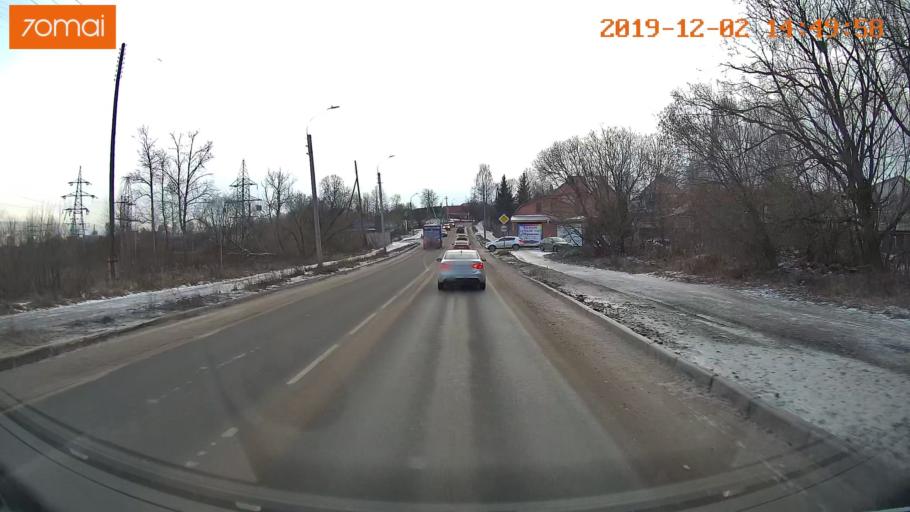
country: RU
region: Ivanovo
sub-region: Gorod Ivanovo
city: Ivanovo
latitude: 56.9833
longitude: 41.0083
